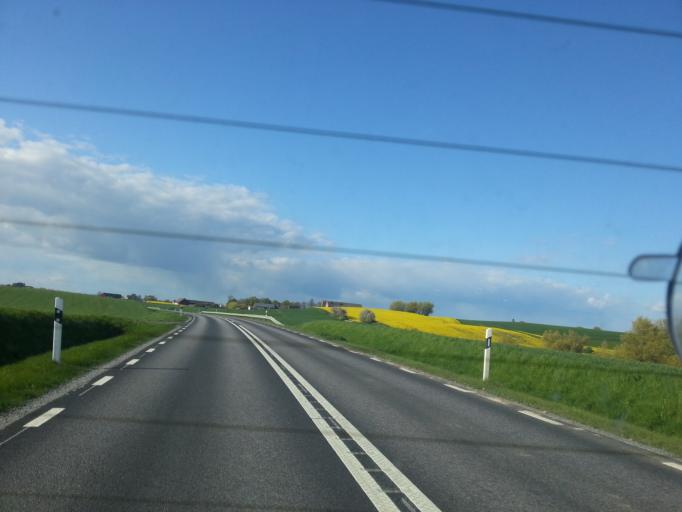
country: SE
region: Skane
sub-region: Ystads Kommun
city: Ystad
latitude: 55.4629
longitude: 13.7987
